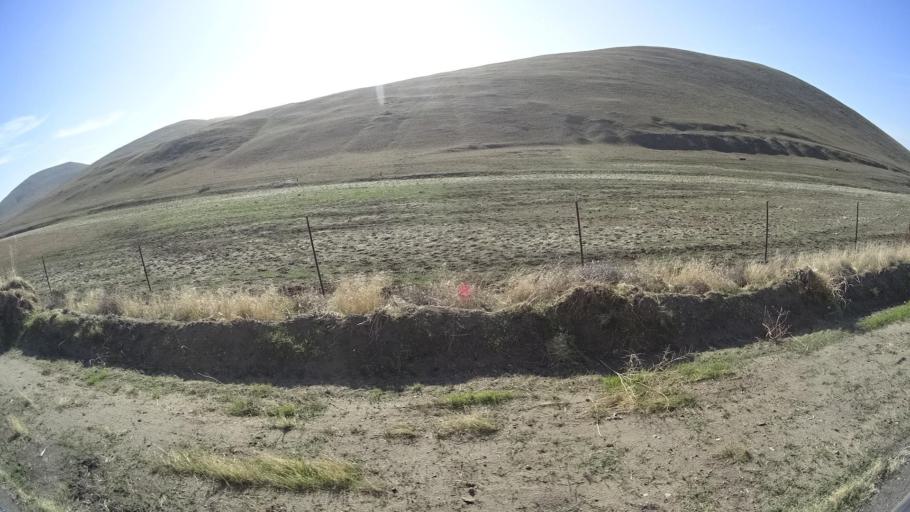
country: US
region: California
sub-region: Kern County
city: Lamont
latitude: 35.3802
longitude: -118.8307
